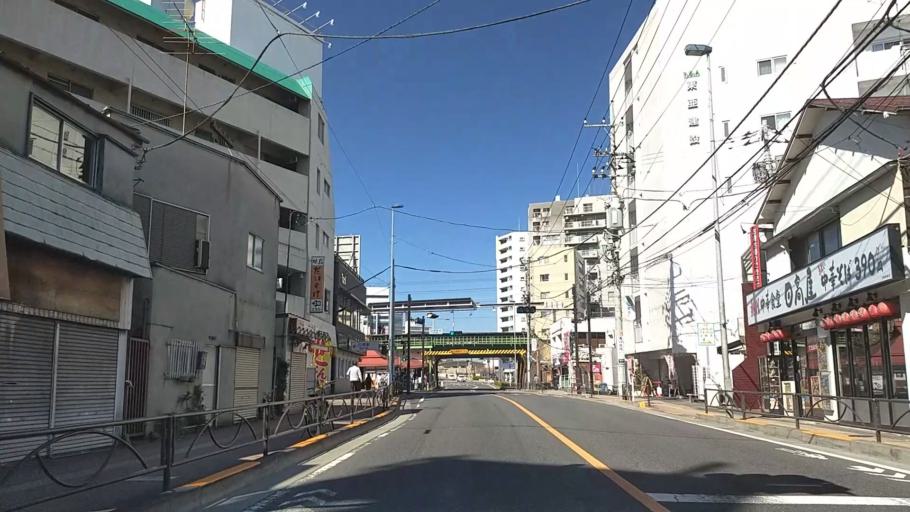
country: JP
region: Tokyo
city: Hino
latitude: 35.6795
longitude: 139.3952
